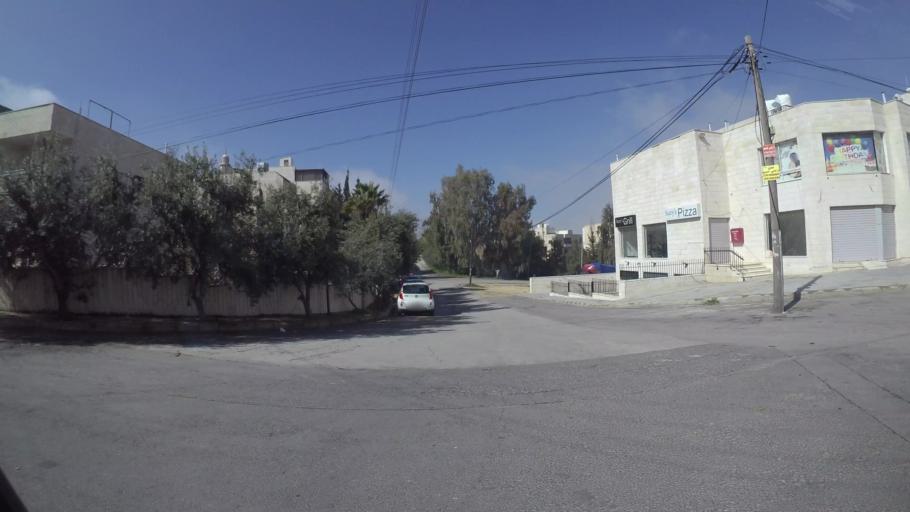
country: JO
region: Amman
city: Umm as Summaq
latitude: 31.8995
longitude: 35.8656
